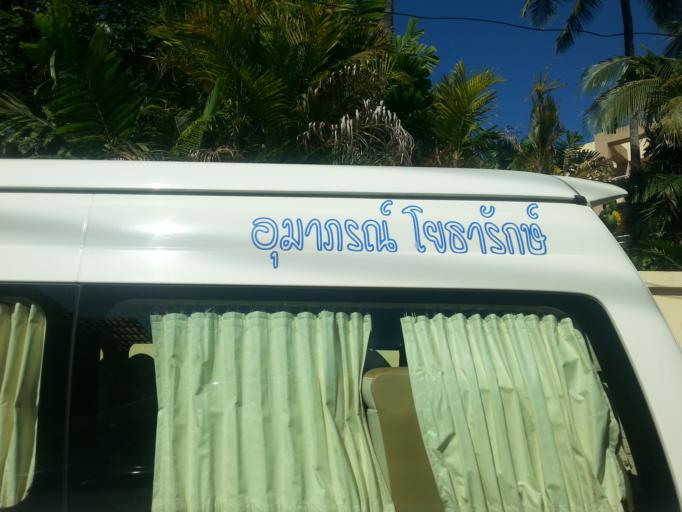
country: TH
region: Phuket
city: Patong
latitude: 7.8882
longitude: 98.2928
